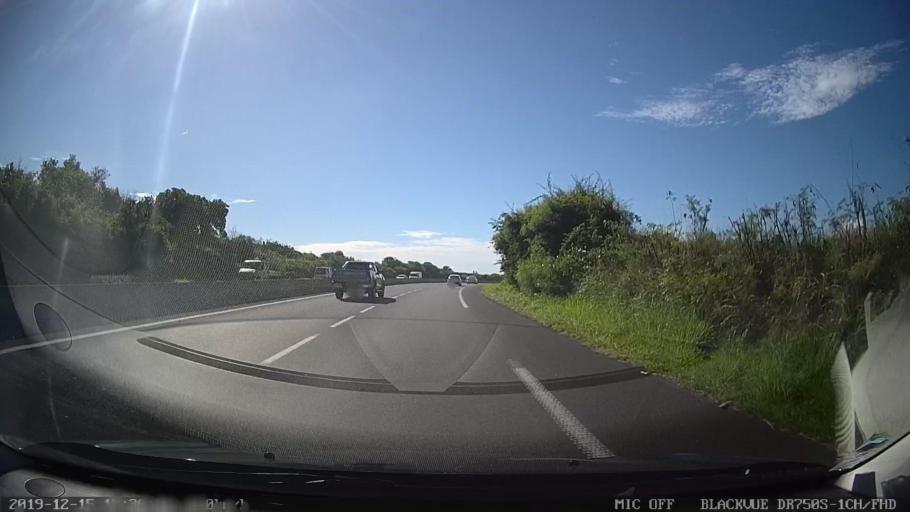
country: RE
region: Reunion
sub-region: Reunion
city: Saint-Pierre
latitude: -21.3182
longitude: 55.4446
